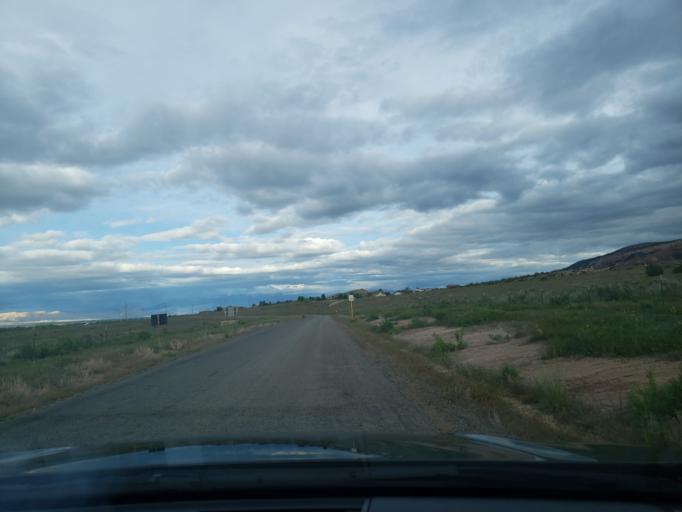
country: US
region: Colorado
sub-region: Mesa County
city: Fruita
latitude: 39.1406
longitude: -108.7537
